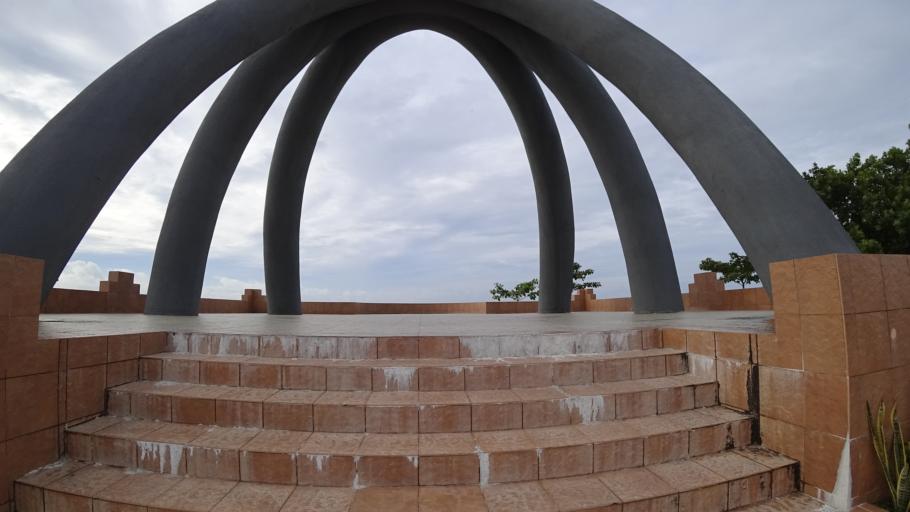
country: BN
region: Belait
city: Seria
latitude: 4.6167
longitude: 114.3172
